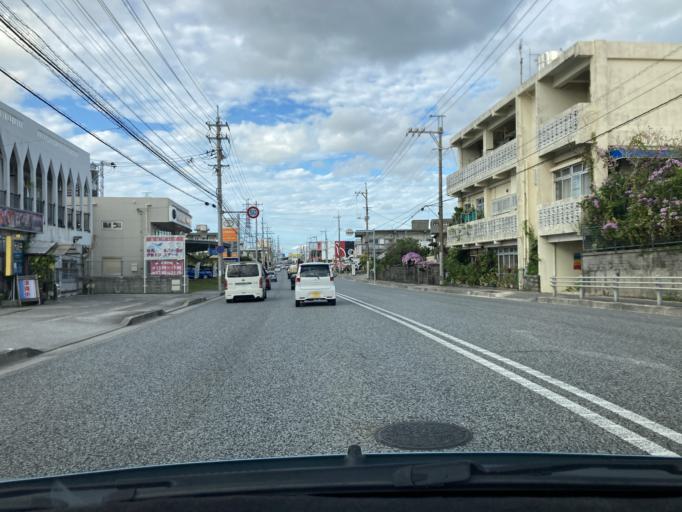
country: JP
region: Okinawa
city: Ishikawa
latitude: 26.3819
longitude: 127.8277
